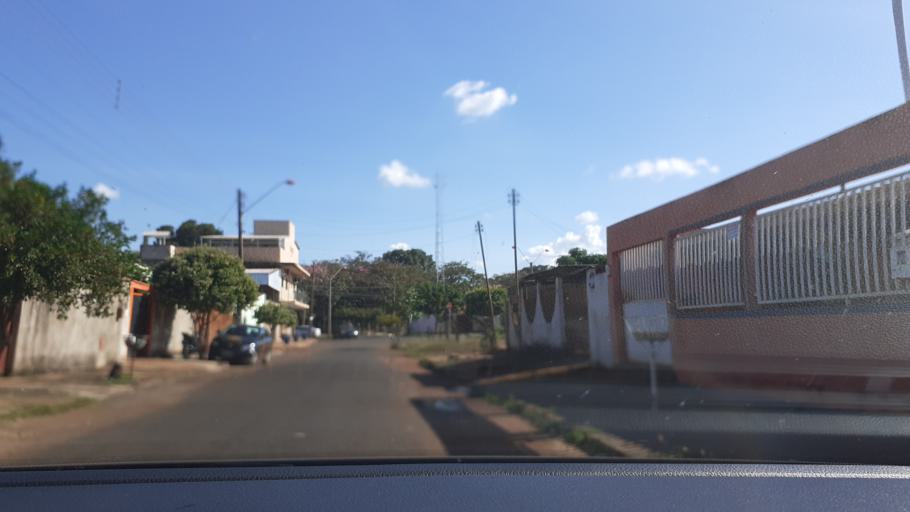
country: BR
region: Goias
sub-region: Itumbiara
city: Itumbiara
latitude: -18.4135
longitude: -49.2569
